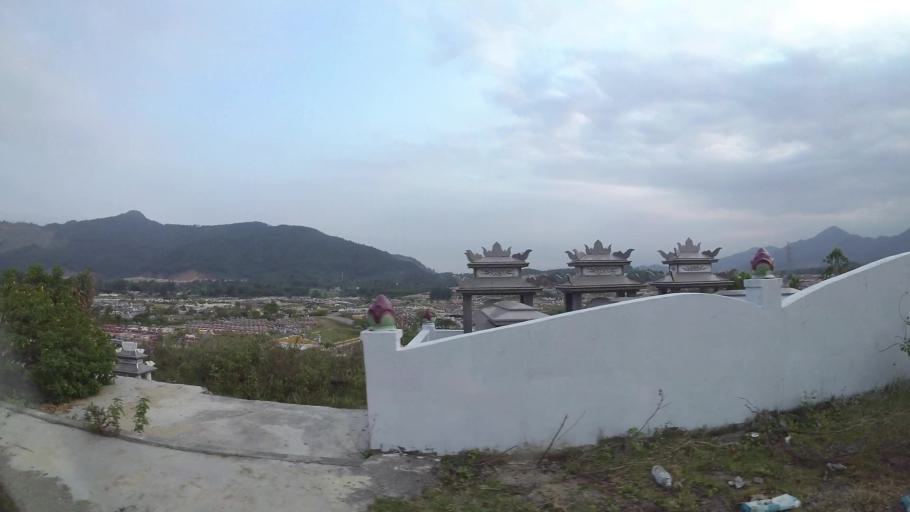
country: VN
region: Da Nang
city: Lien Chieu
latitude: 16.0623
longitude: 108.1130
